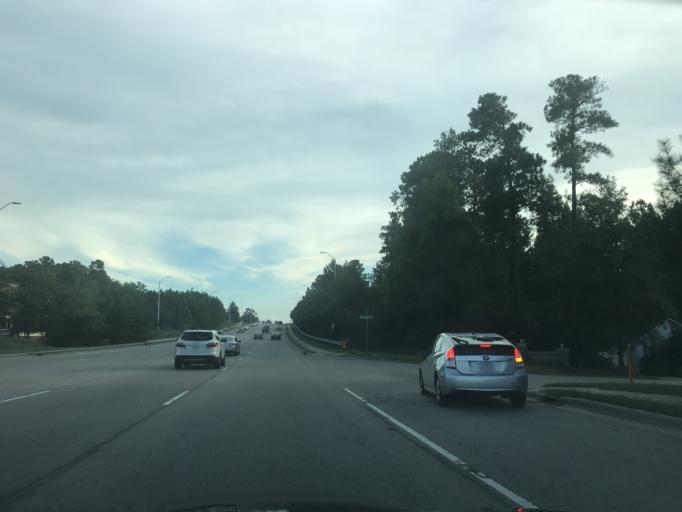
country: US
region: North Carolina
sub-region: Wake County
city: Green Level
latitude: 35.7935
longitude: -78.8706
